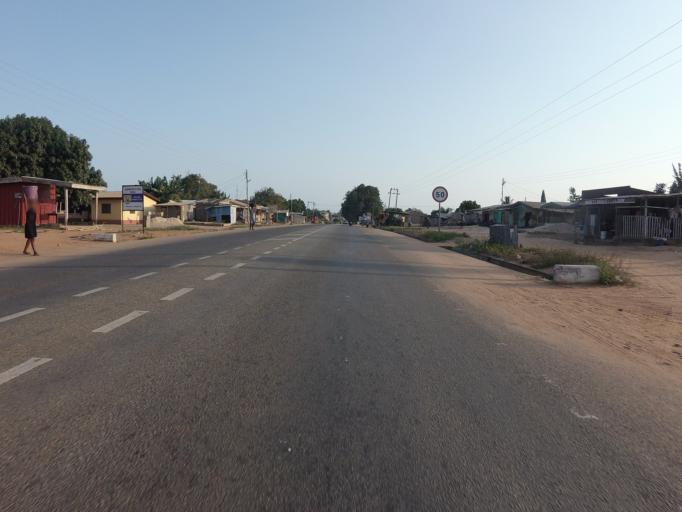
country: GH
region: Volta
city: Anloga
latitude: 6.0099
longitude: 0.5966
